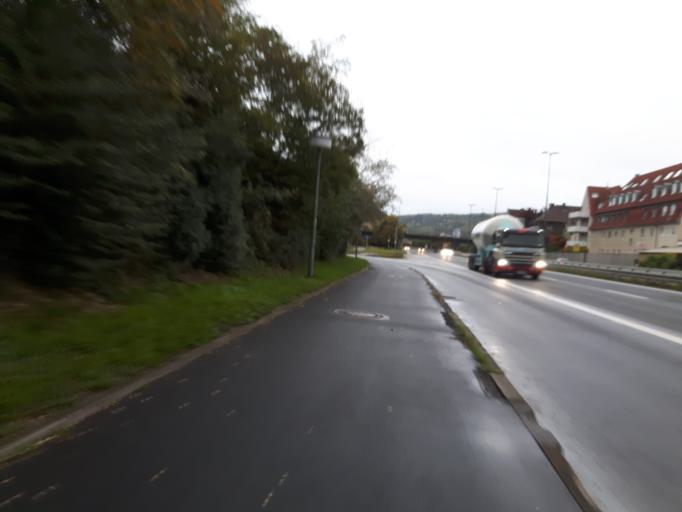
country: DE
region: Bavaria
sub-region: Regierungsbezirk Unterfranken
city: Zell am Main
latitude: 49.8096
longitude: 9.8837
